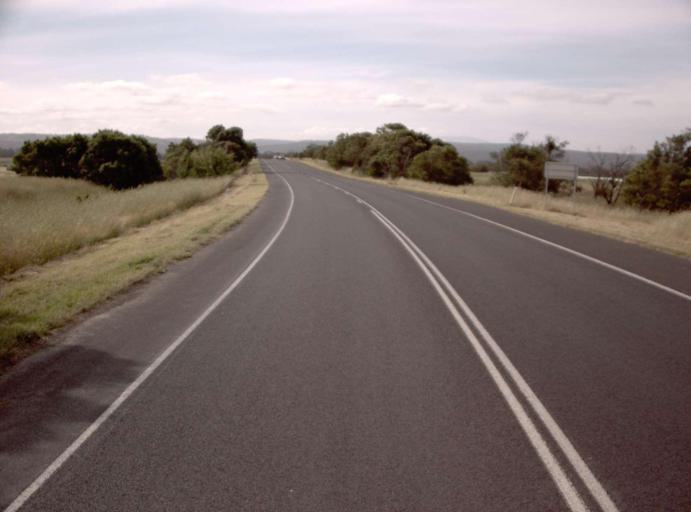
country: AU
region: Victoria
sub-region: Latrobe
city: Traralgon
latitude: -38.1672
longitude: 146.5633
